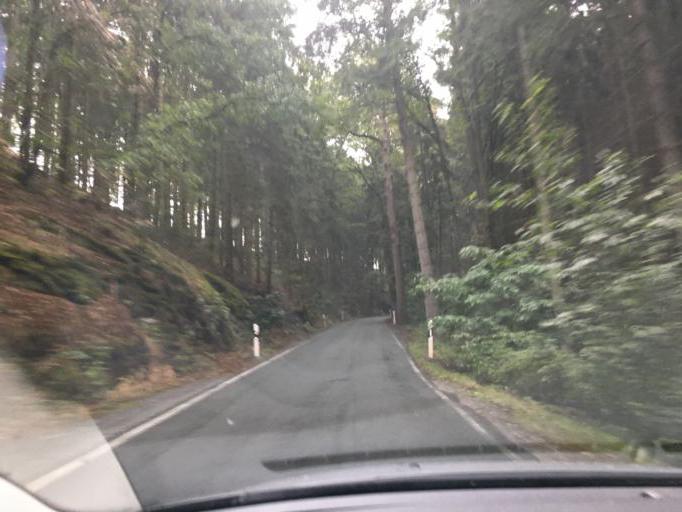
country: DE
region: Thuringia
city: Burgk
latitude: 50.5514
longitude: 11.7297
